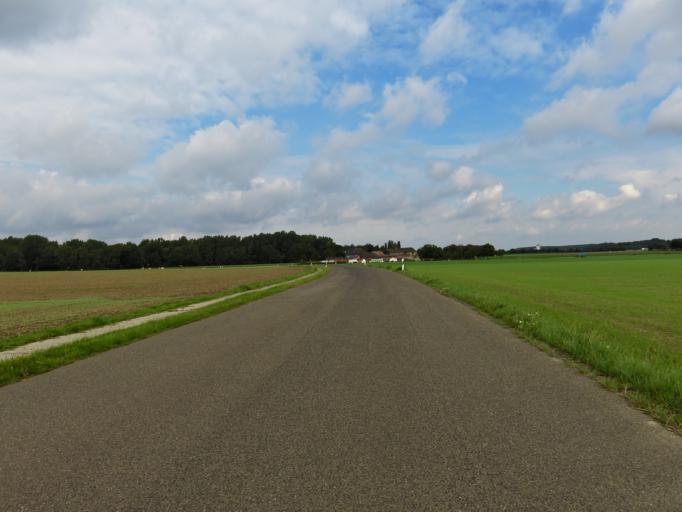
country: DE
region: North Rhine-Westphalia
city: Geilenkirchen
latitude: 50.9631
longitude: 6.0732
